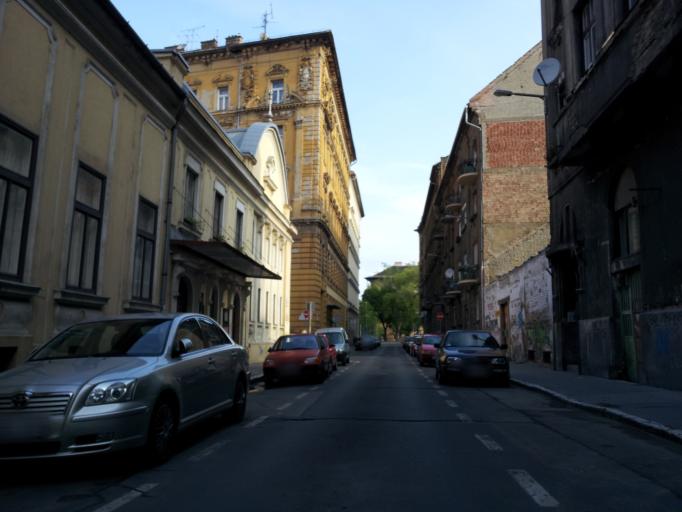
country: HU
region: Budapest
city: Budapest VIII. keruelet
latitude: 47.4912
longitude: 19.0721
